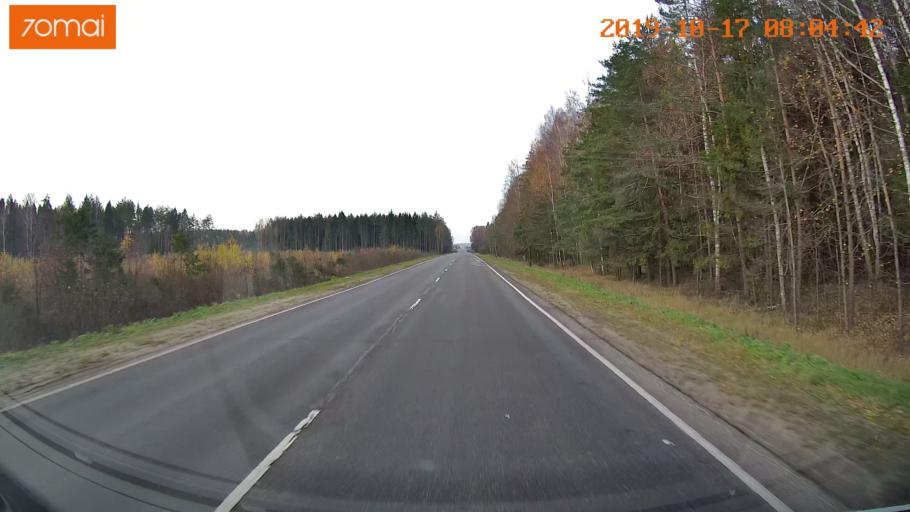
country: RU
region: Vladimir
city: Belaya Rechka
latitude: 56.3425
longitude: 39.4301
